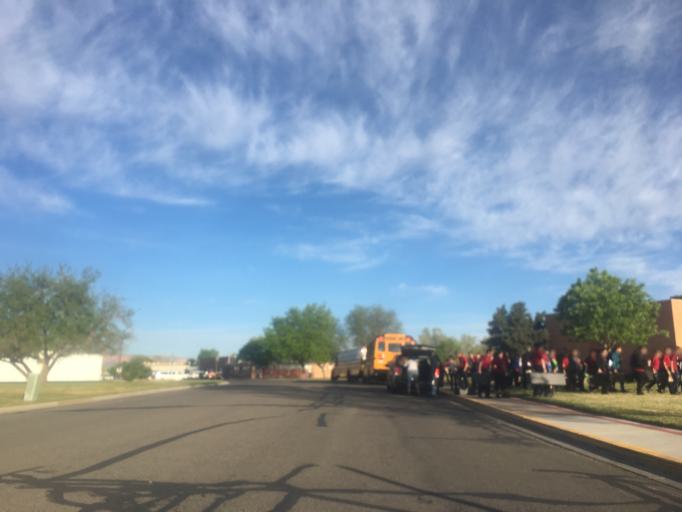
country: US
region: Colorado
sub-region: Mesa County
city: Grand Junction
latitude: 39.0788
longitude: -108.5631
